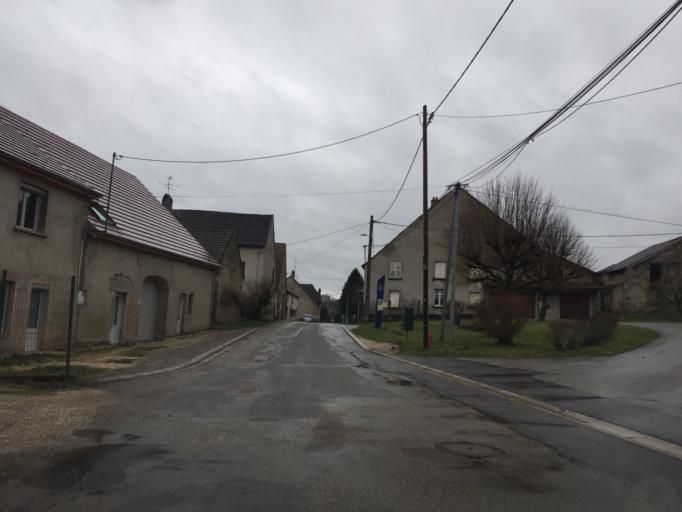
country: FR
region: Franche-Comte
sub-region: Departement du Jura
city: Champvans
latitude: 47.1458
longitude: 5.4578
